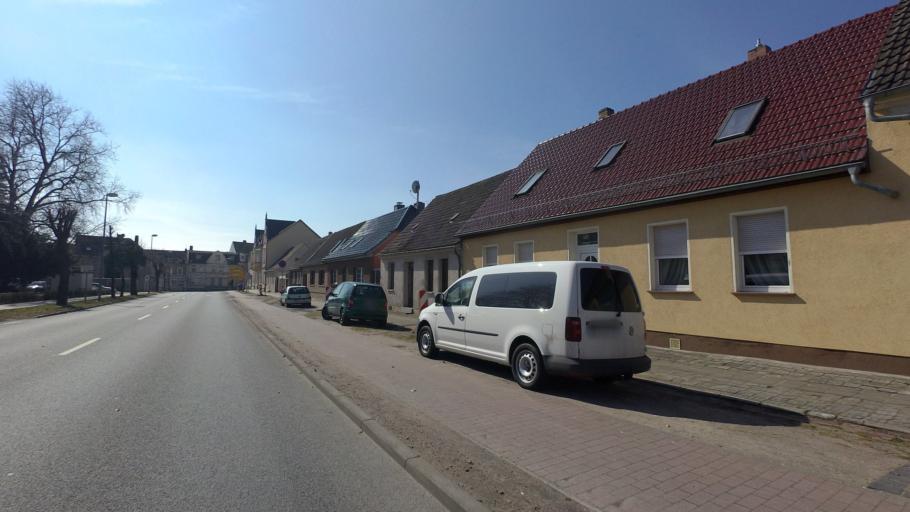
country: DE
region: Saxony-Anhalt
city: Coswig
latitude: 51.8840
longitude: 12.4486
